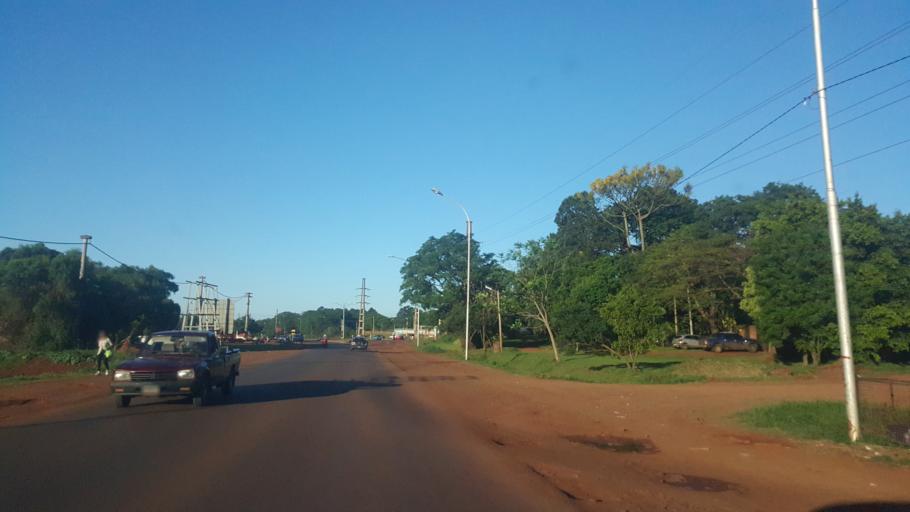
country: AR
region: Misiones
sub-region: Departamento de Capital
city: Posadas
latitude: -27.4268
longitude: -55.9356
